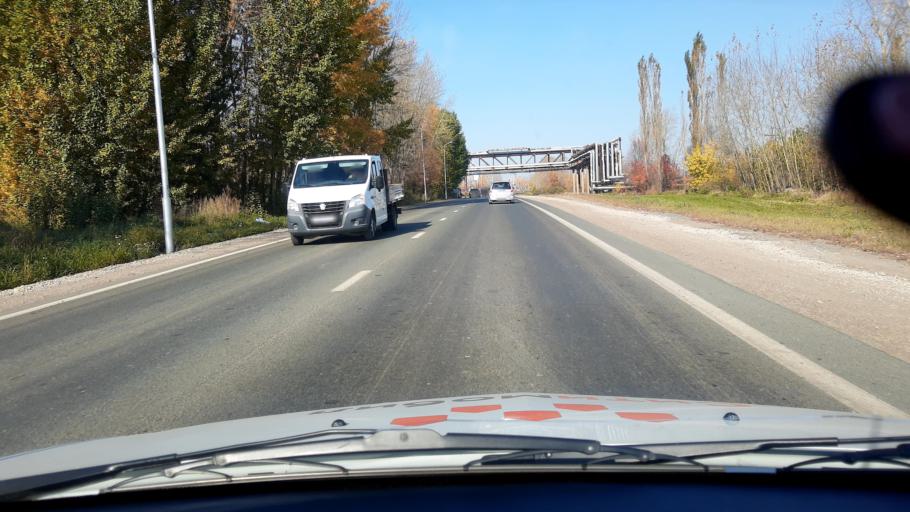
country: RU
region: Bashkortostan
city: Ufa
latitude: 54.8438
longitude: 56.1215
